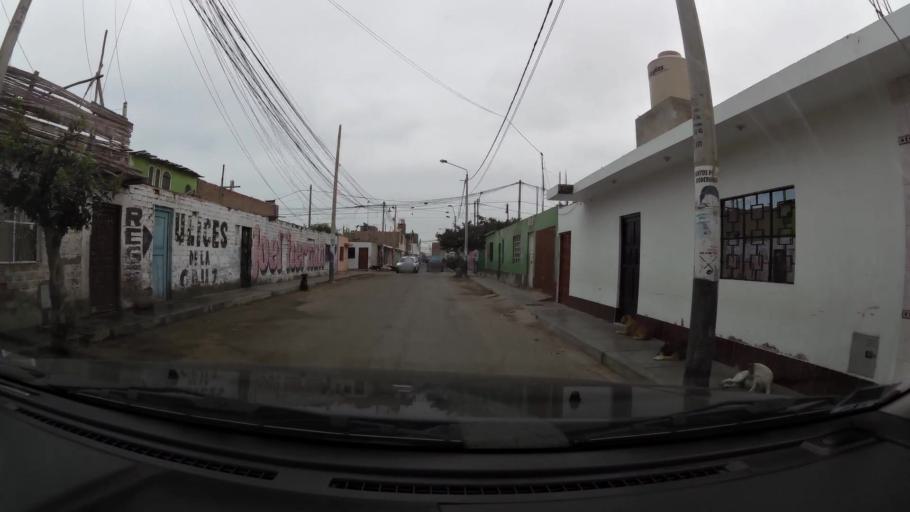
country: PE
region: Ica
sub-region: Provincia de Pisco
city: Pisco
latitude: -13.7362
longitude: -76.2226
